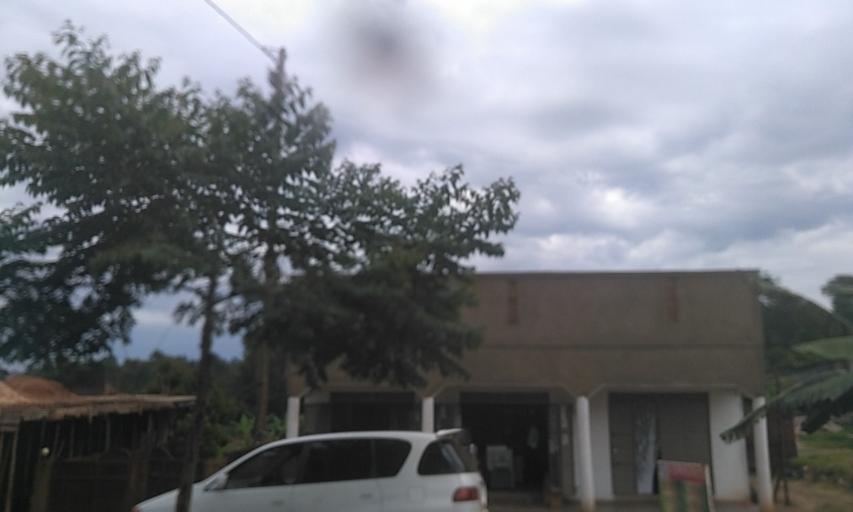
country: UG
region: Central Region
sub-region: Wakiso District
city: Bweyogerere
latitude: 0.3945
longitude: 32.6890
